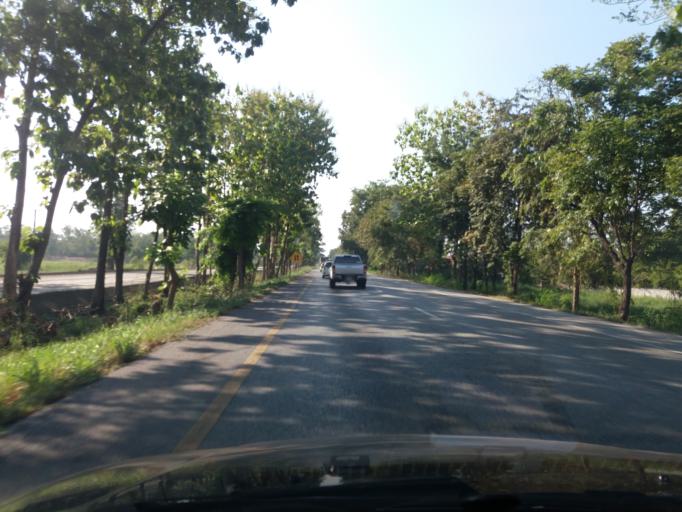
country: TH
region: Nakhon Sawan
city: Nakhon Sawan
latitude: 15.7379
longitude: 100.0201
